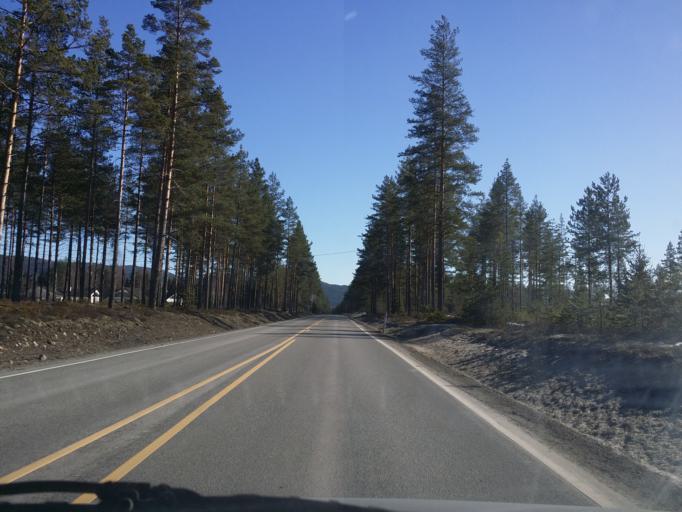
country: NO
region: Buskerud
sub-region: Ringerike
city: Honefoss
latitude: 60.3114
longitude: 10.1553
